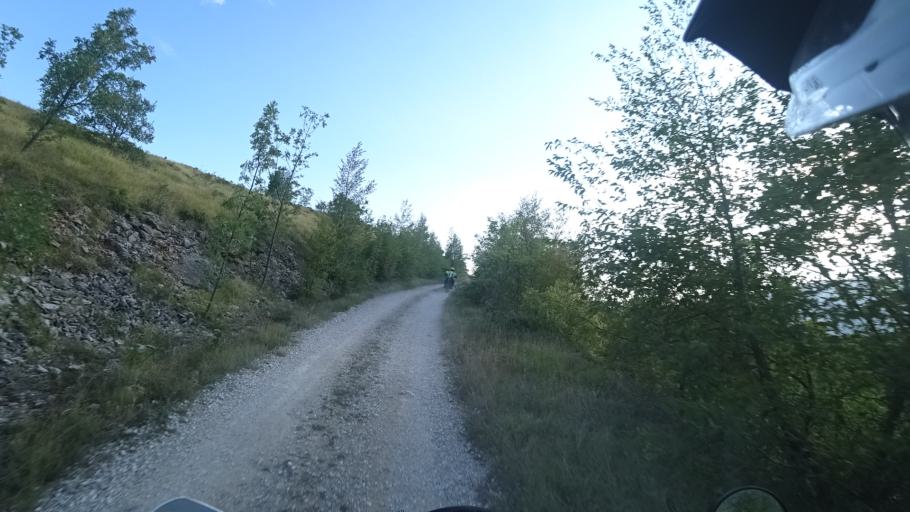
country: HR
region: Sibensko-Kniniska
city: Knin
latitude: 44.1371
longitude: 16.1201
